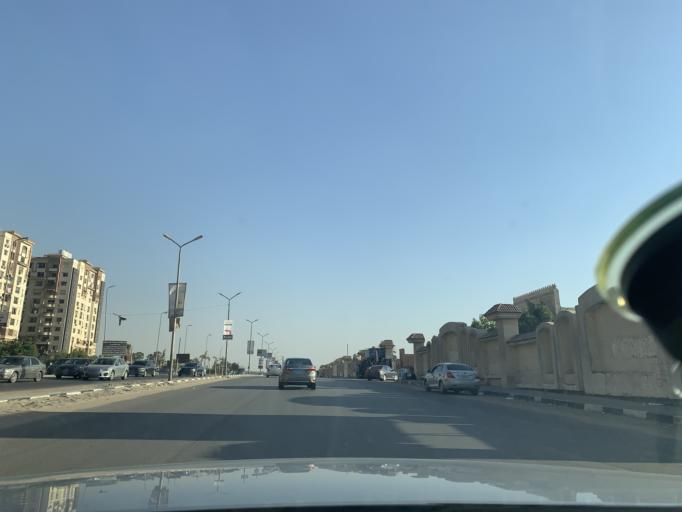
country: EG
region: Muhafazat al Qahirah
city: Cairo
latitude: 30.0329
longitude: 31.3546
